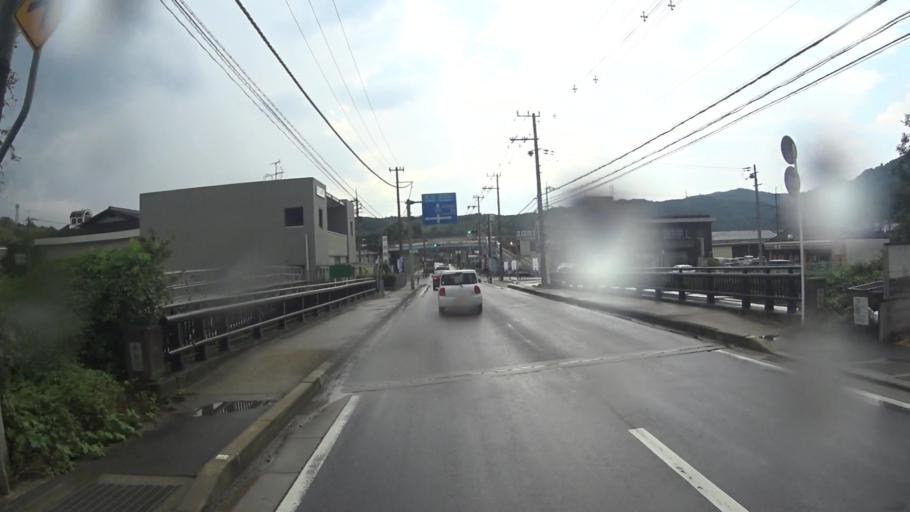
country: JP
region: Kyoto
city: Uji
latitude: 34.8503
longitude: 135.8544
